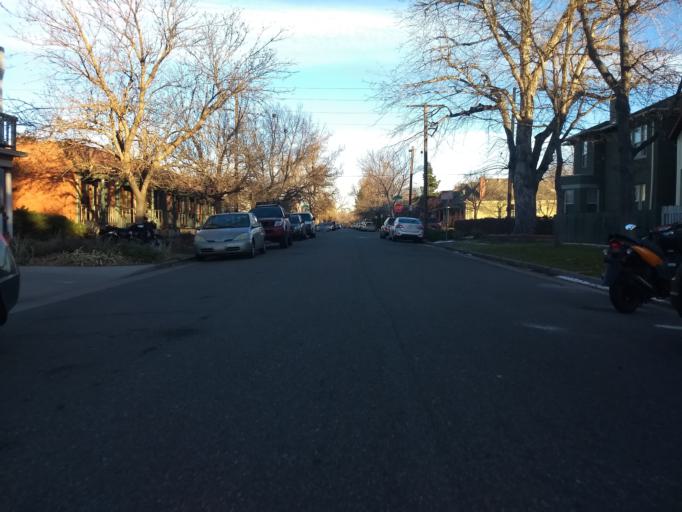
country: US
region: Colorado
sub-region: Denver County
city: Denver
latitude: 39.7139
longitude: -104.9907
